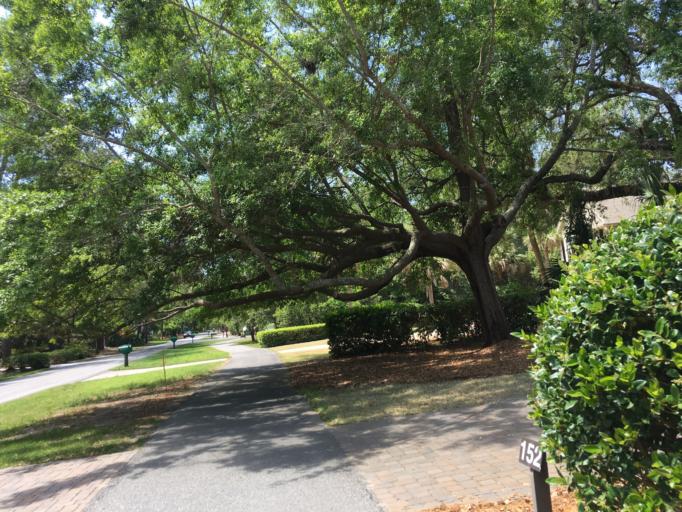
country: US
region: South Carolina
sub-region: Beaufort County
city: Hilton Head Island
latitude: 32.1227
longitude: -80.7975
